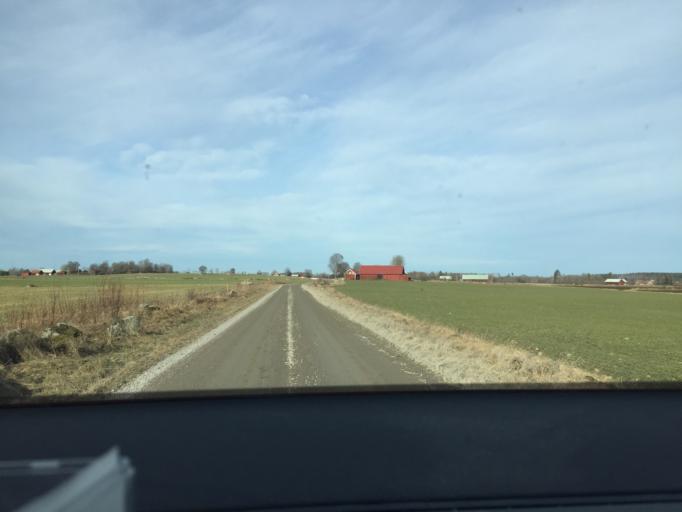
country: SE
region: OErebro
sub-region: Hallsbergs Kommun
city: Skollersta
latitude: 59.1283
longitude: 15.4308
